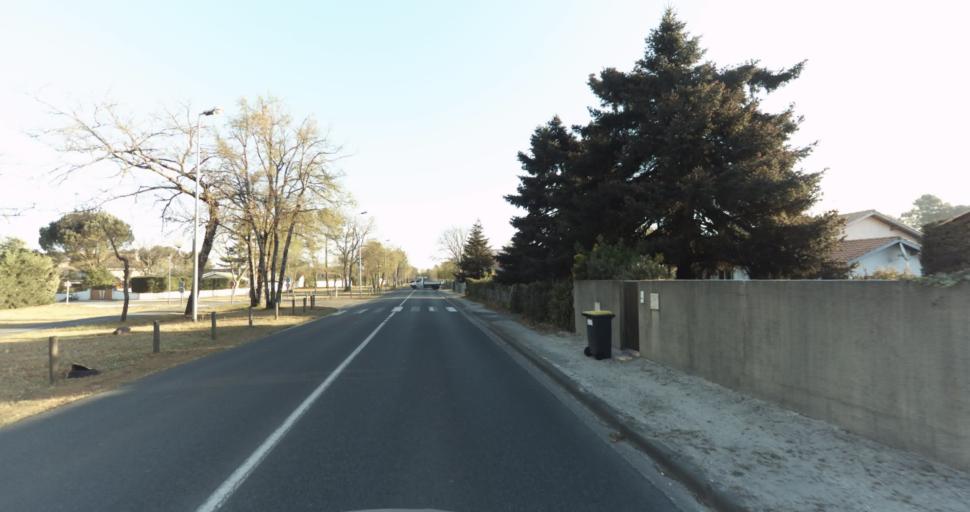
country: FR
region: Aquitaine
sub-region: Departement de la Gironde
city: Martignas-sur-Jalle
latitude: 44.8157
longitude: -0.7796
